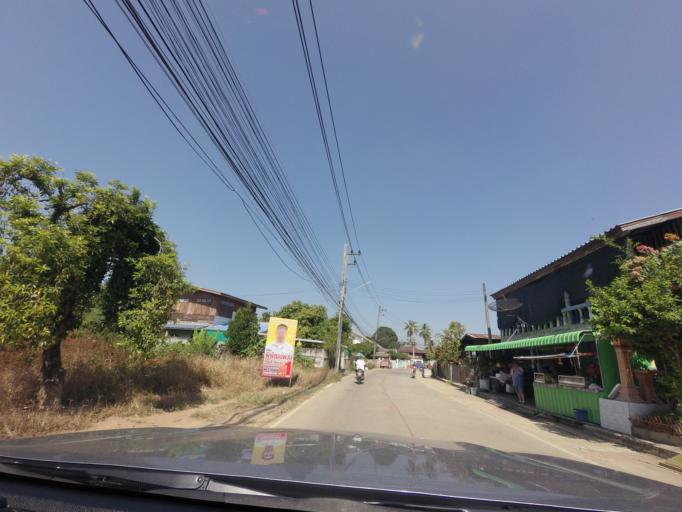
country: TH
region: Sukhothai
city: Sawankhalok
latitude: 17.3153
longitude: 99.8245
